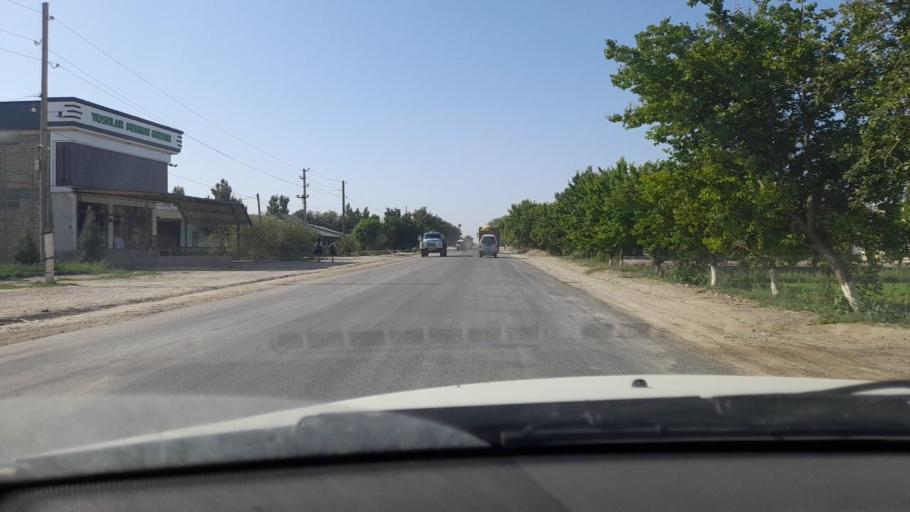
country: UZ
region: Bukhara
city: Romiton
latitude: 40.0571
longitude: 64.3278
